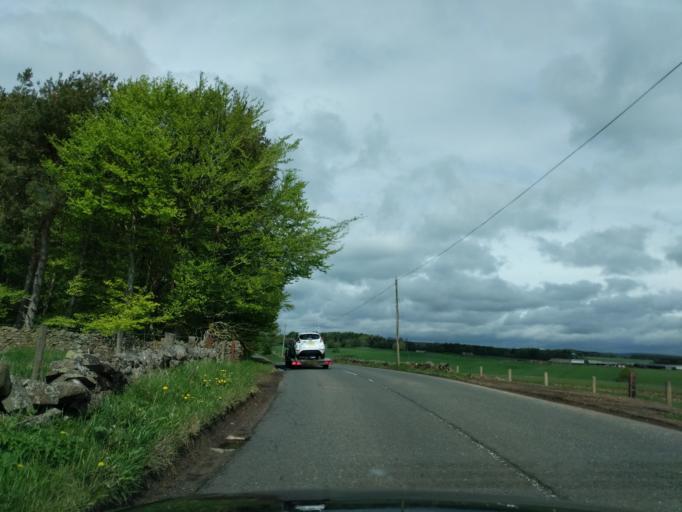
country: GB
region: Scotland
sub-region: The Scottish Borders
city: Earlston
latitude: 55.6953
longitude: -2.5814
